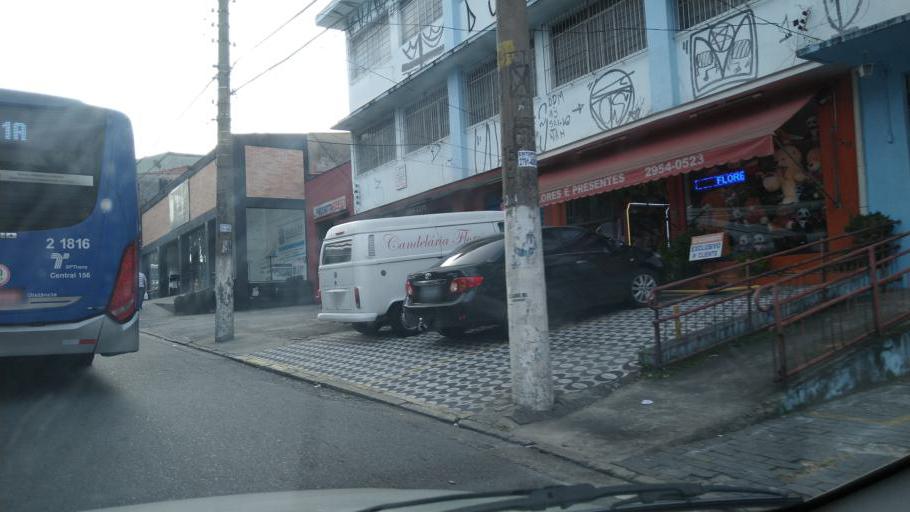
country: BR
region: Sao Paulo
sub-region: Sao Paulo
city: Sao Paulo
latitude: -23.5123
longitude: -46.5853
